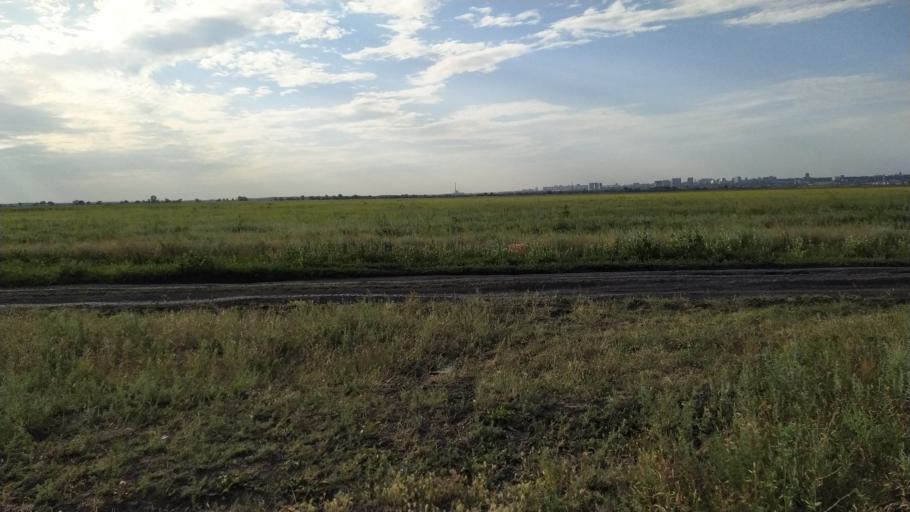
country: RU
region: Rostov
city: Kuleshovka
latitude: 47.1380
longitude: 39.6349
